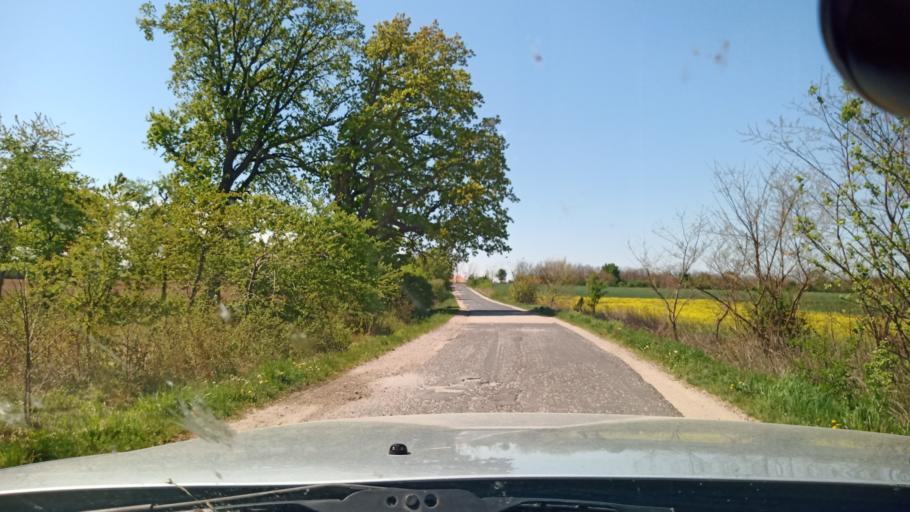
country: HU
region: Zala
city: Heviz
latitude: 46.7663
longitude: 17.1523
